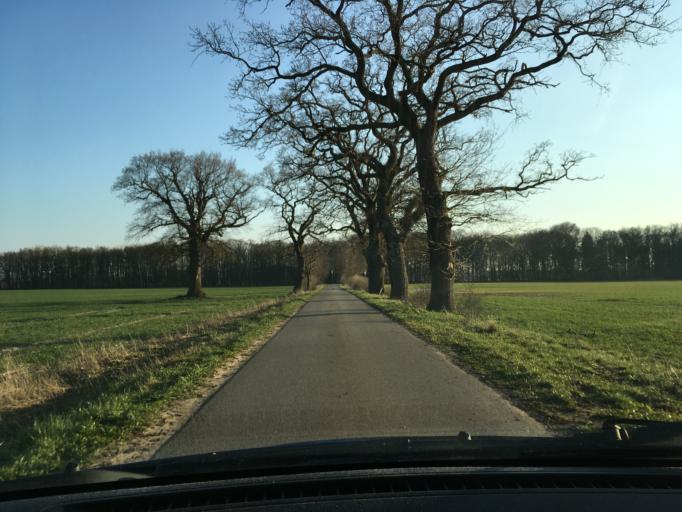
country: DE
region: Lower Saxony
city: Hittbergen
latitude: 53.3229
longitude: 10.6278
